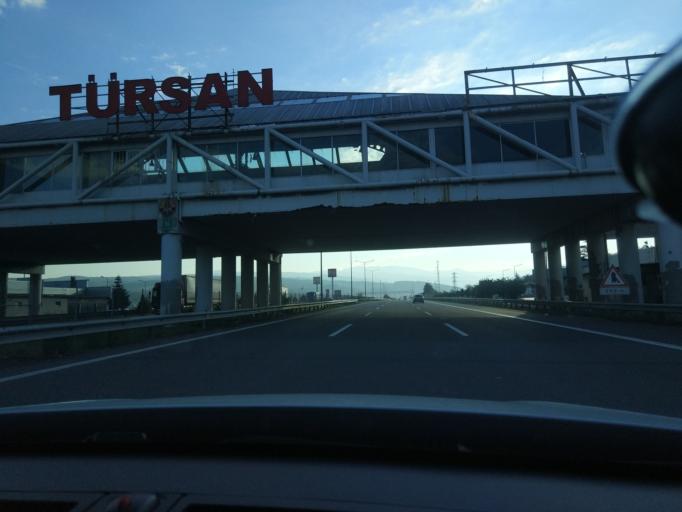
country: TR
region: Duzce
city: Kaynasli
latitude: 40.7904
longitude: 31.2403
